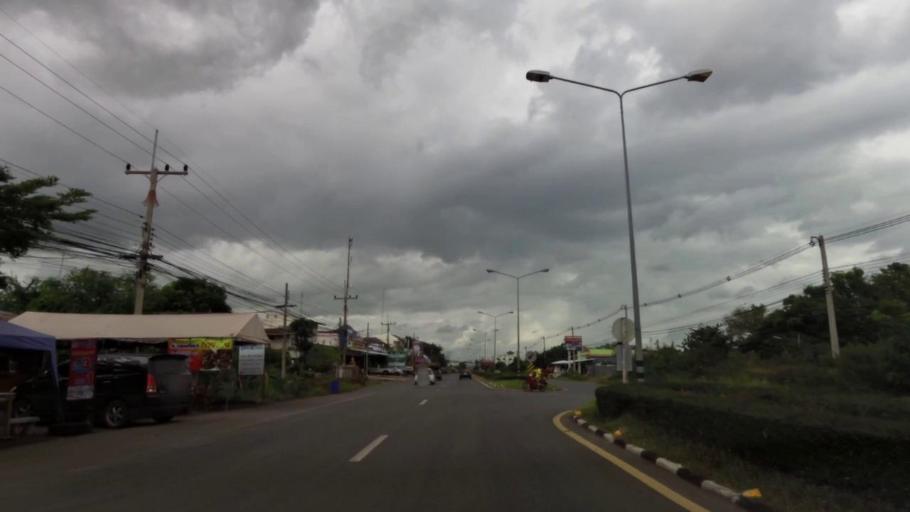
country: TH
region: Nakhon Sawan
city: Phai Sali
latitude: 15.5934
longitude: 100.6519
